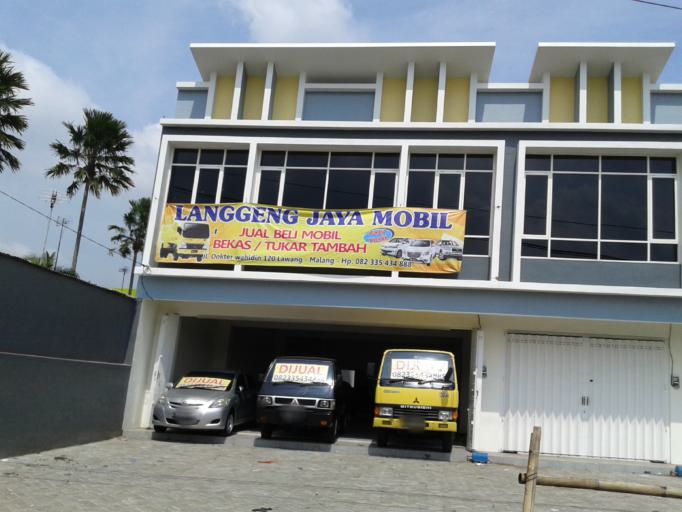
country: ID
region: East Java
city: Lawang
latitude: -7.8521
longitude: 112.6942
